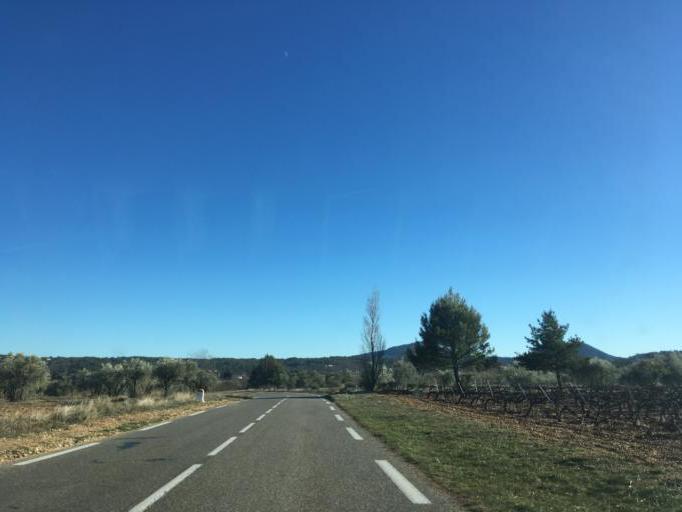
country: FR
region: Provence-Alpes-Cote d'Azur
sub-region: Departement du Var
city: Barjols
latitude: 43.5943
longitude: 5.9990
